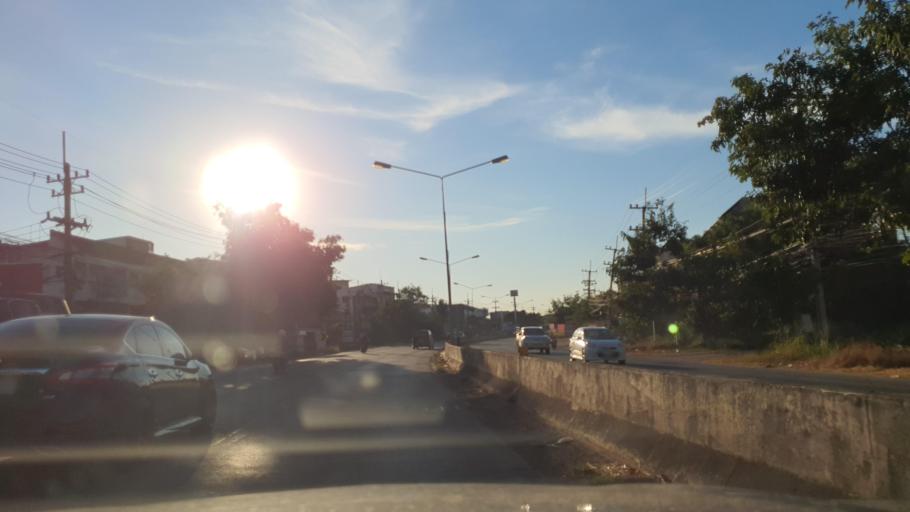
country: TH
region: Khon Kaen
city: Khon Kaen
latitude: 16.4266
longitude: 102.8821
